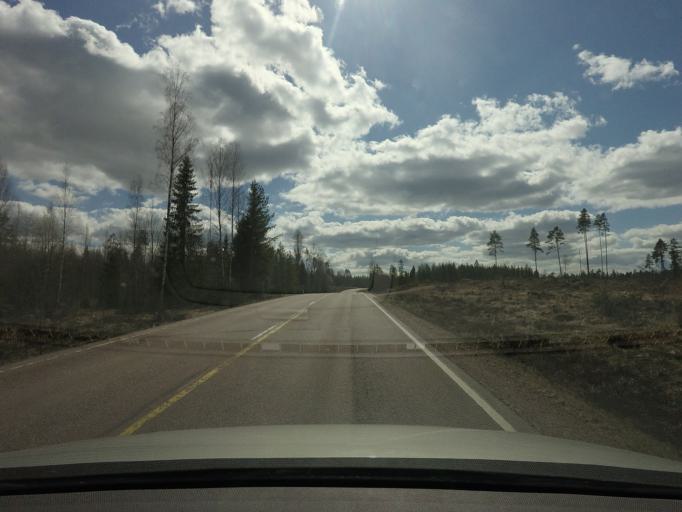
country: FI
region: Kymenlaakso
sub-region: Kotka-Hamina
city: Hamina
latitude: 60.7341
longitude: 27.3296
